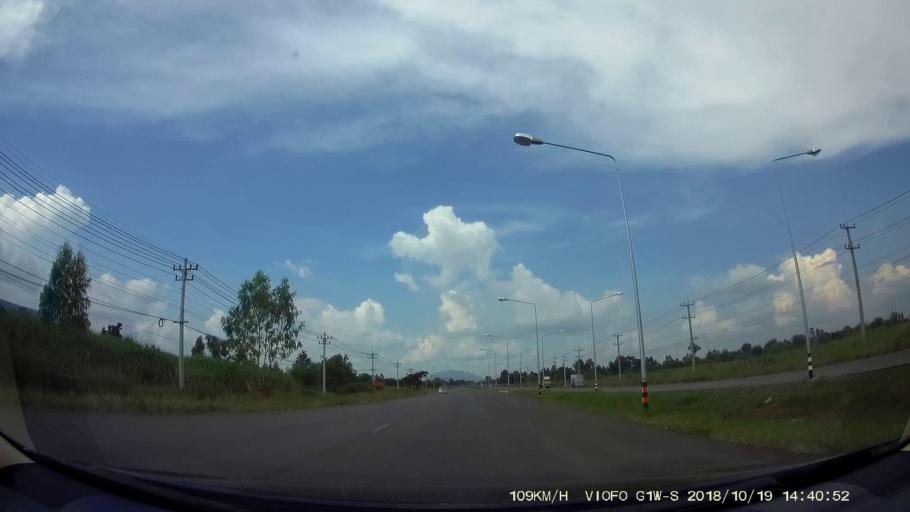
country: TH
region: Chaiyaphum
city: Phu Khiao
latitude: 16.2475
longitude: 102.1973
